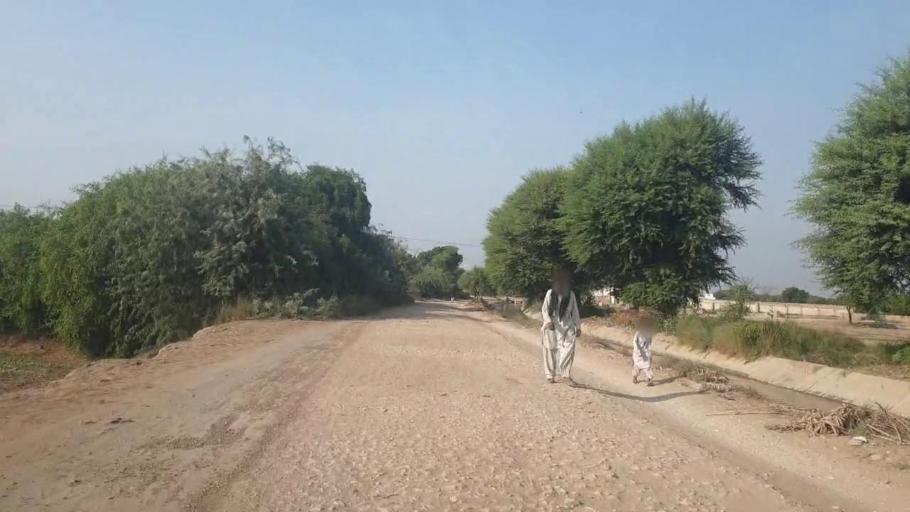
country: PK
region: Sindh
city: Tando Jam
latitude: 25.4147
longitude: 68.4645
